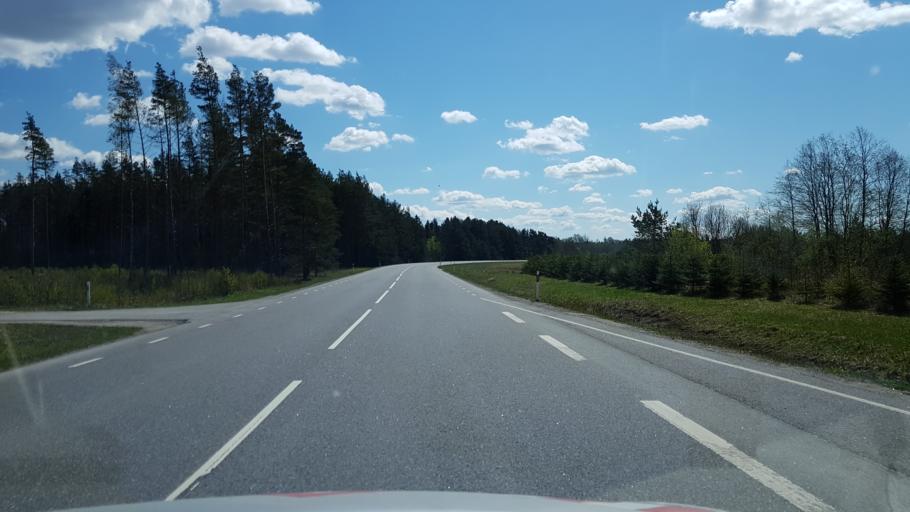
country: EE
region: Harju
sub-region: Paldiski linn
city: Paldiski
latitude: 59.2578
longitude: 24.1515
